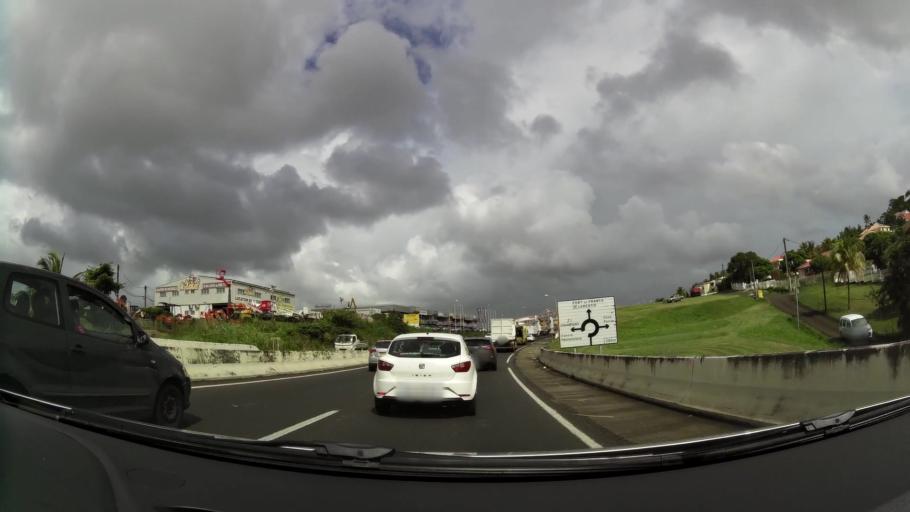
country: MQ
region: Martinique
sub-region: Martinique
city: Ducos
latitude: 14.5753
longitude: -60.9852
